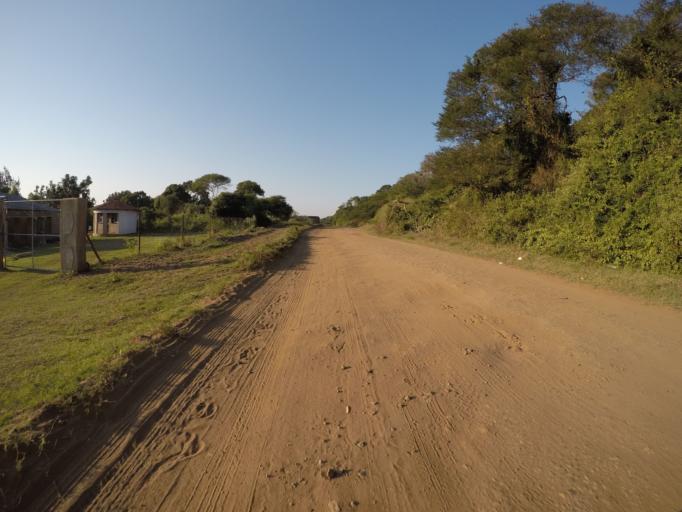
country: ZA
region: KwaZulu-Natal
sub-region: uThungulu District Municipality
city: KwaMbonambi
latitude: -28.7064
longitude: 32.1859
